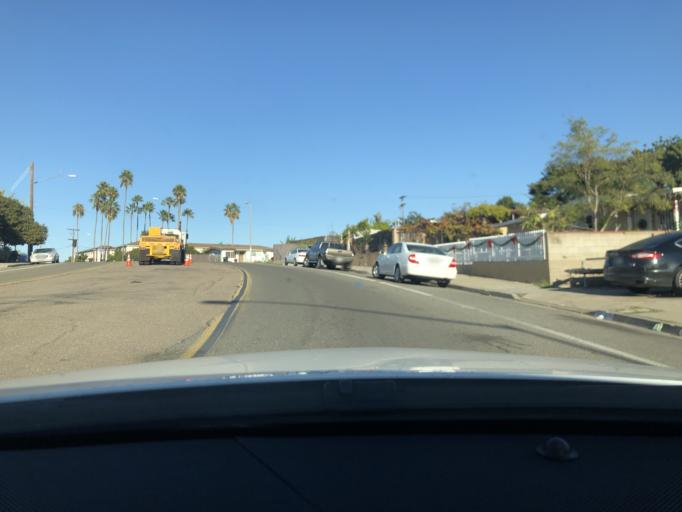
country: US
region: California
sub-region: San Diego County
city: Lemon Grove
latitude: 32.7447
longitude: -117.0594
